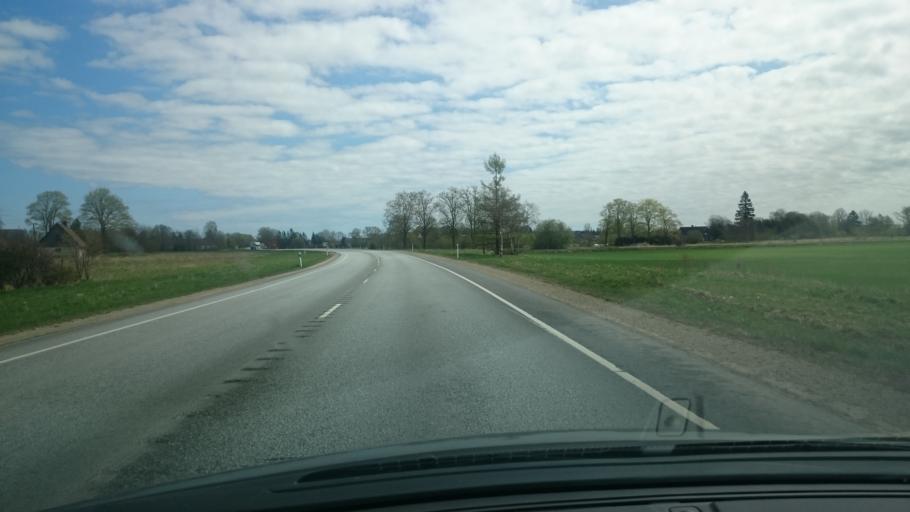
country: EE
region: Ida-Virumaa
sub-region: Puessi linn
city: Pussi
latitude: 59.4031
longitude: 27.0853
